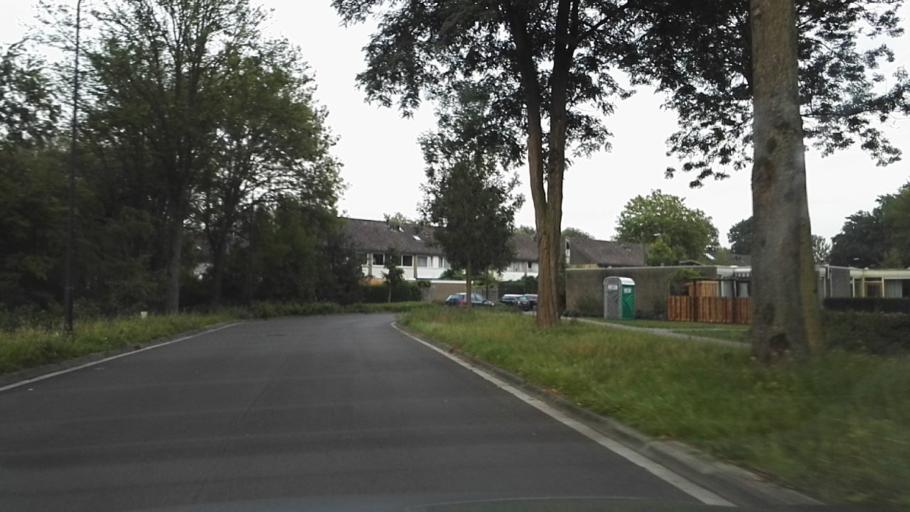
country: NL
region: Gelderland
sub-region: Gemeente Apeldoorn
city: Apeldoorn
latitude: 52.2030
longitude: 6.0008
